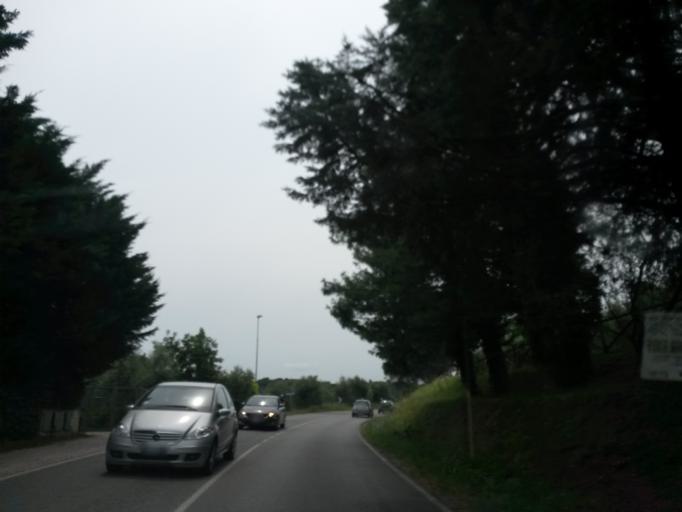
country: IT
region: Lombardy
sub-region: Provincia di Brescia
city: Salo
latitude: 45.6016
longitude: 10.5078
